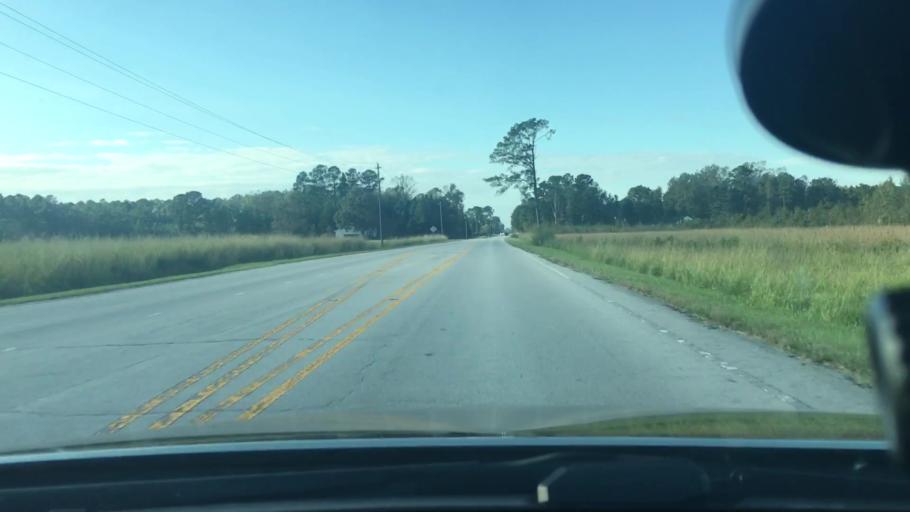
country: US
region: North Carolina
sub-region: Craven County
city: Vanceboro
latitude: 35.3531
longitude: -77.1899
